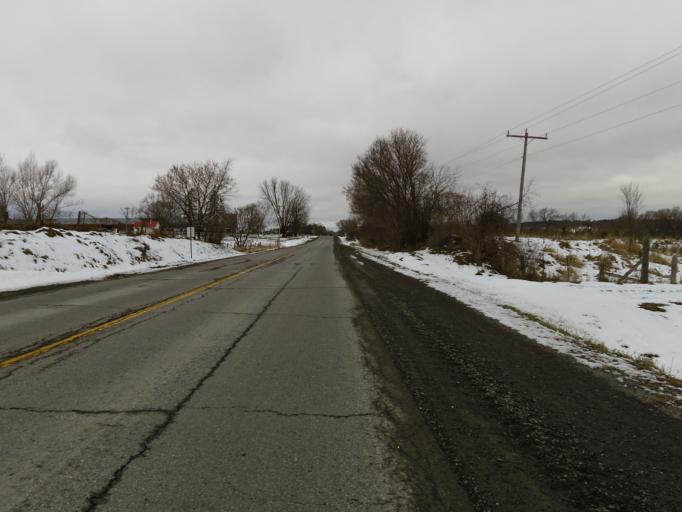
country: CA
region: Ontario
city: Bells Corners
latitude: 45.3403
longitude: -76.0541
